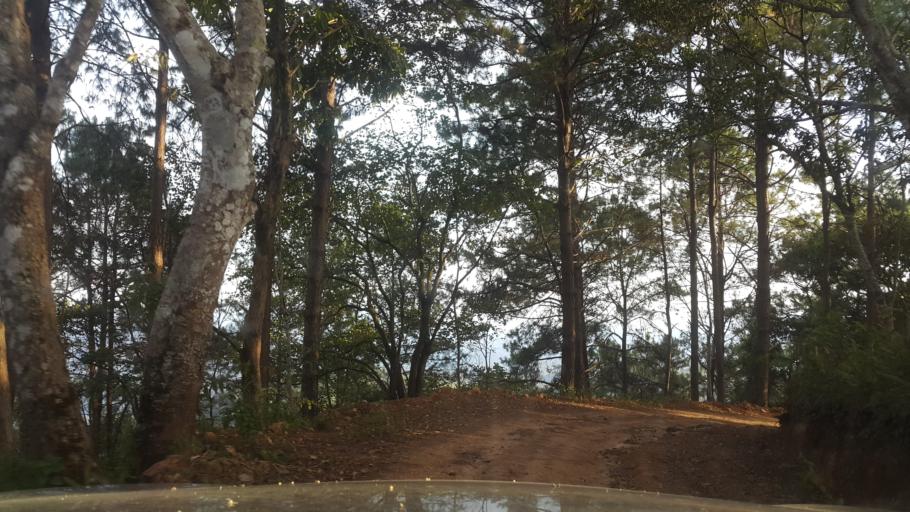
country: TH
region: Chiang Mai
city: Samoeng
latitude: 19.0288
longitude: 98.6472
